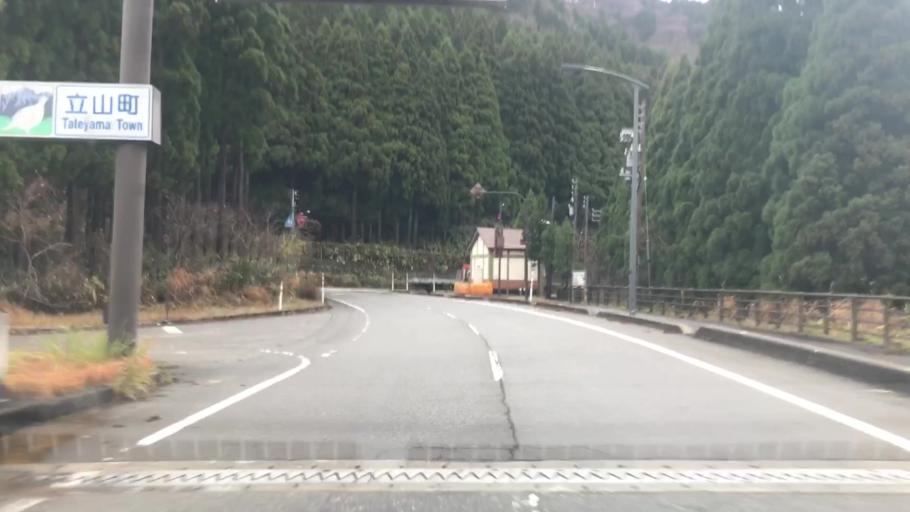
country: JP
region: Toyama
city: Kamiichi
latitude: 36.5823
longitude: 137.4060
